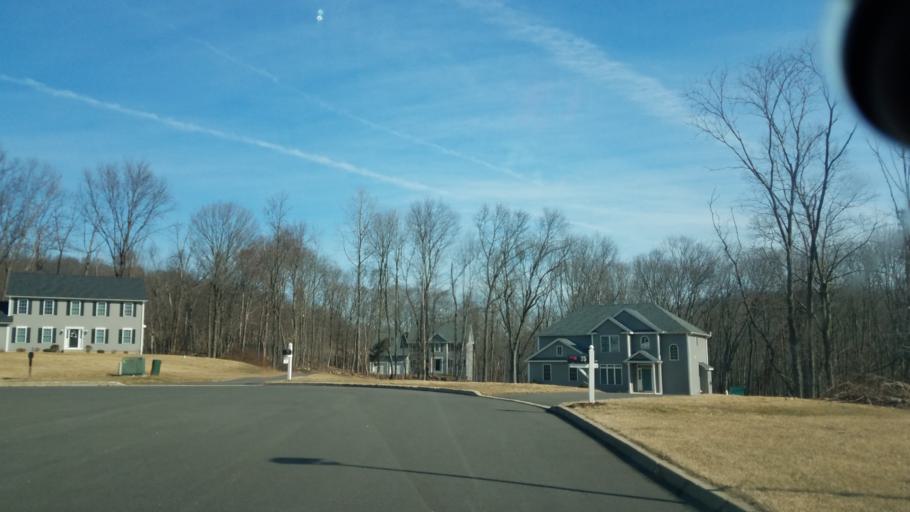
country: US
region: Connecticut
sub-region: New Haven County
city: Prospect
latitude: 41.5351
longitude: -72.9614
